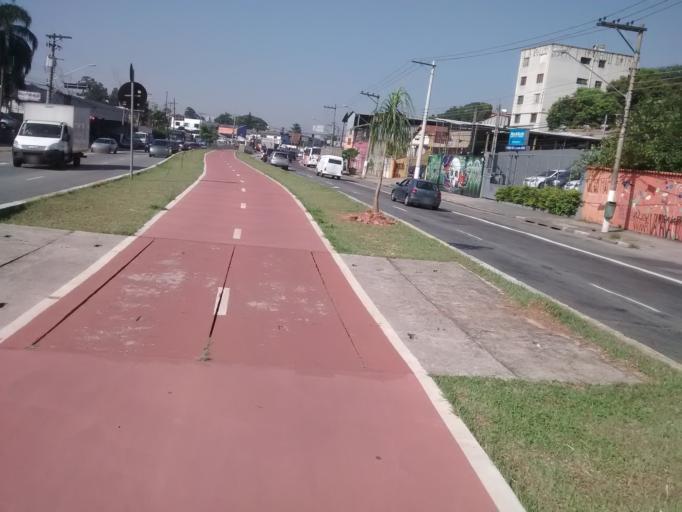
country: BR
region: Sao Paulo
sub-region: Osasco
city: Osasco
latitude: -23.5792
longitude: -46.7197
